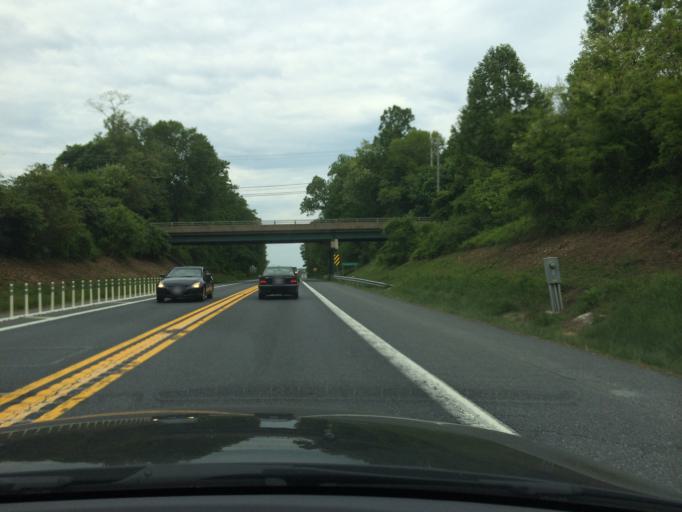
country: US
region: Maryland
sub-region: Howard County
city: Highland
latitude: 39.2634
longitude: -76.9846
